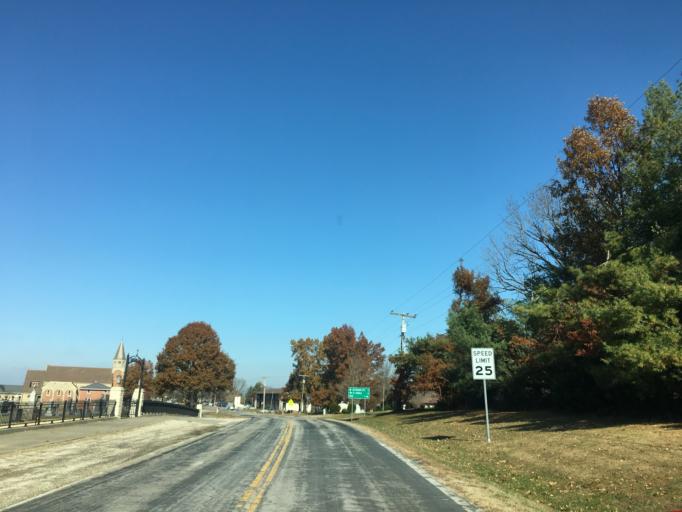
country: US
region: Missouri
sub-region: Cole County
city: Wardsville
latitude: 38.4860
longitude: -92.1756
